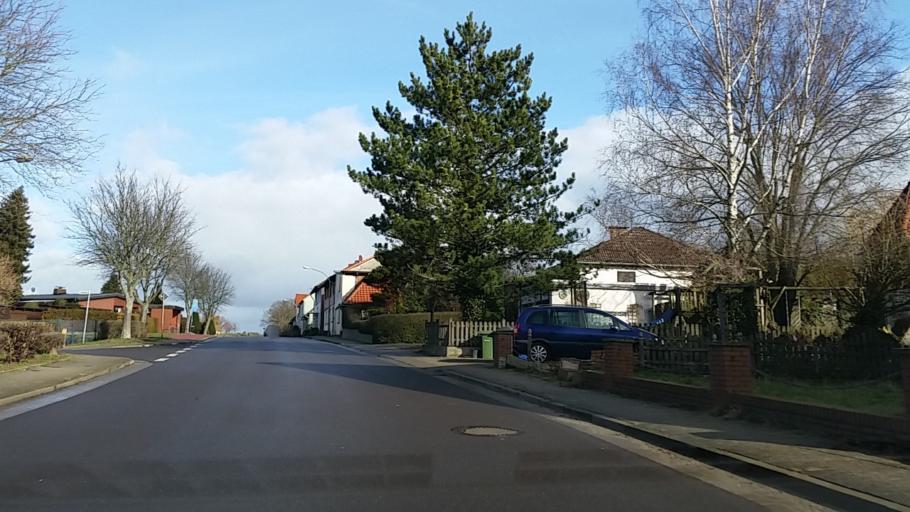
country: DE
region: Lower Saxony
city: Gross Twulpstedt
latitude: 52.3855
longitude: 10.9242
